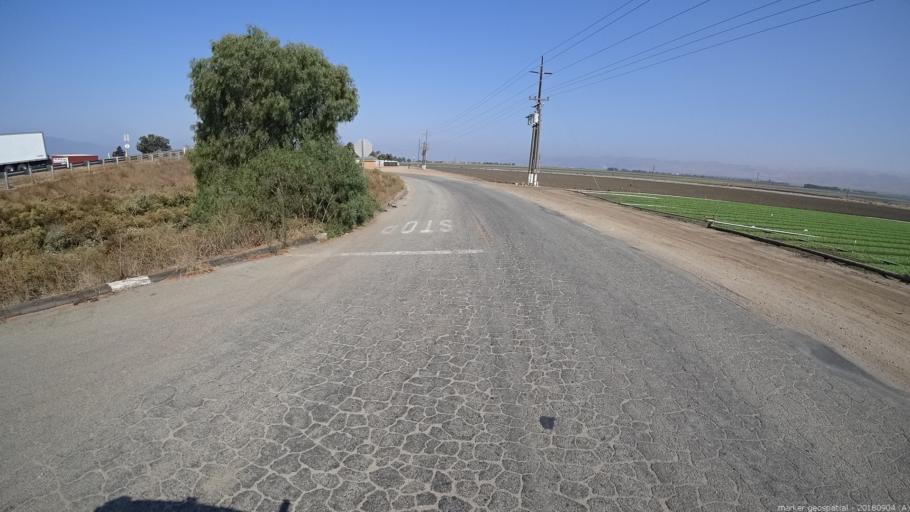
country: US
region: California
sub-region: Monterey County
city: Gonzales
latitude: 36.4926
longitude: -121.4253
